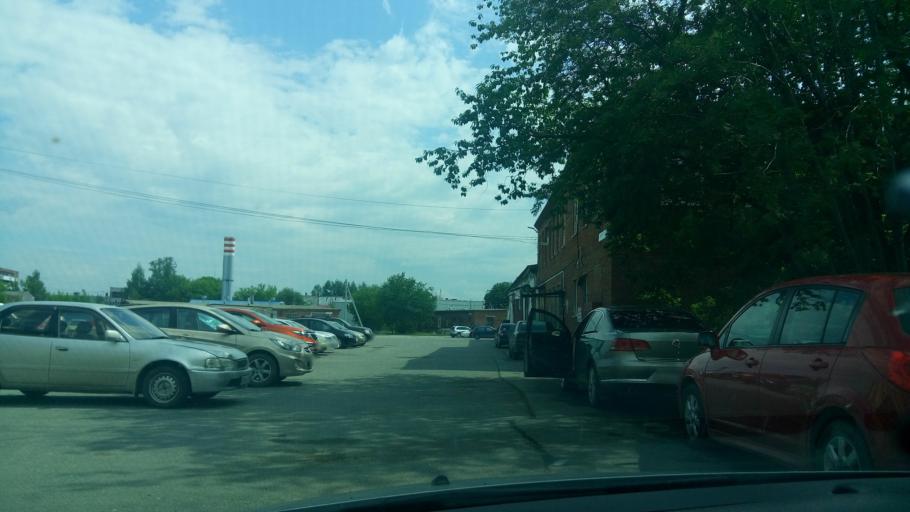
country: RU
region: Sverdlovsk
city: Yekaterinburg
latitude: 56.8564
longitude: 60.6609
